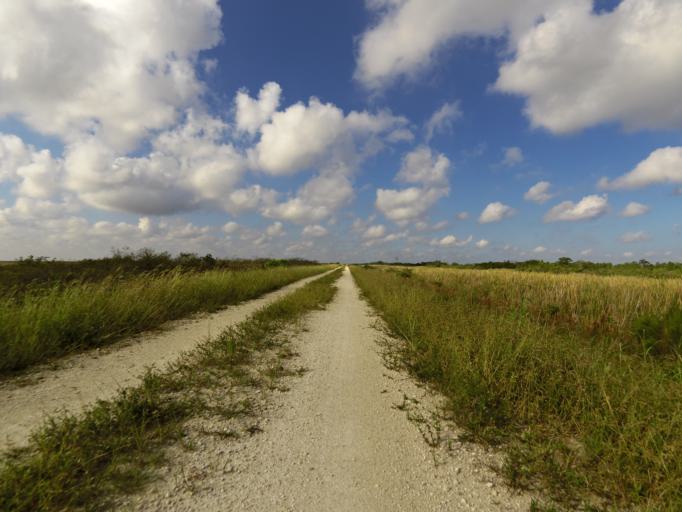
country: US
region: Florida
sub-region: Broward County
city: Weston
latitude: 26.0551
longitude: -80.4603
